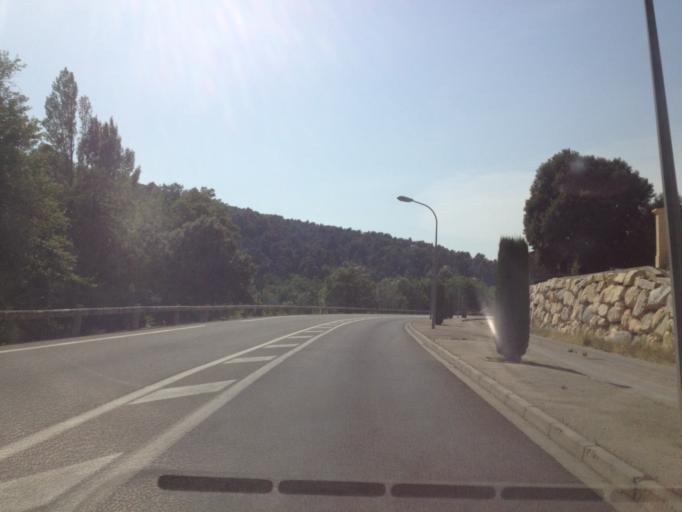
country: FR
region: Provence-Alpes-Cote d'Azur
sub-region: Departement du Vaucluse
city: Vaison-la-Romaine
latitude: 44.2381
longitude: 5.0528
